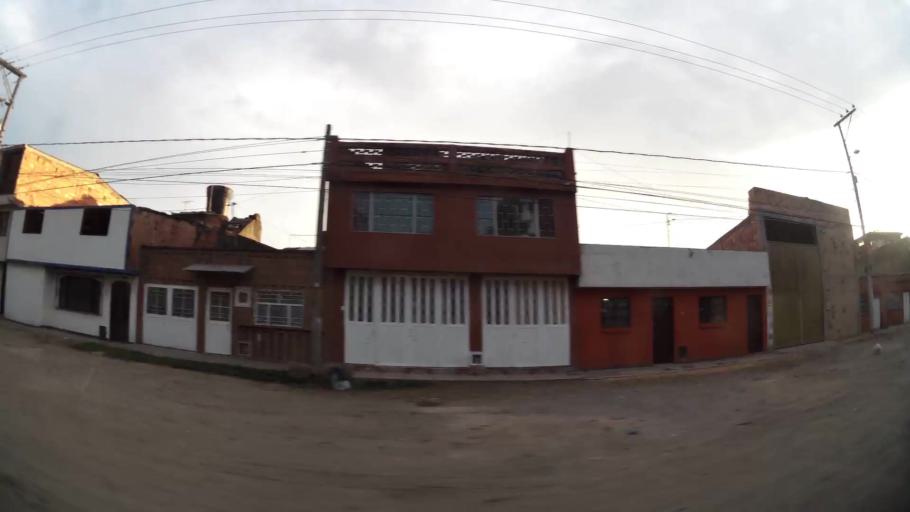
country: CO
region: Cundinamarca
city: Funza
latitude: 4.6968
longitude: -74.1540
